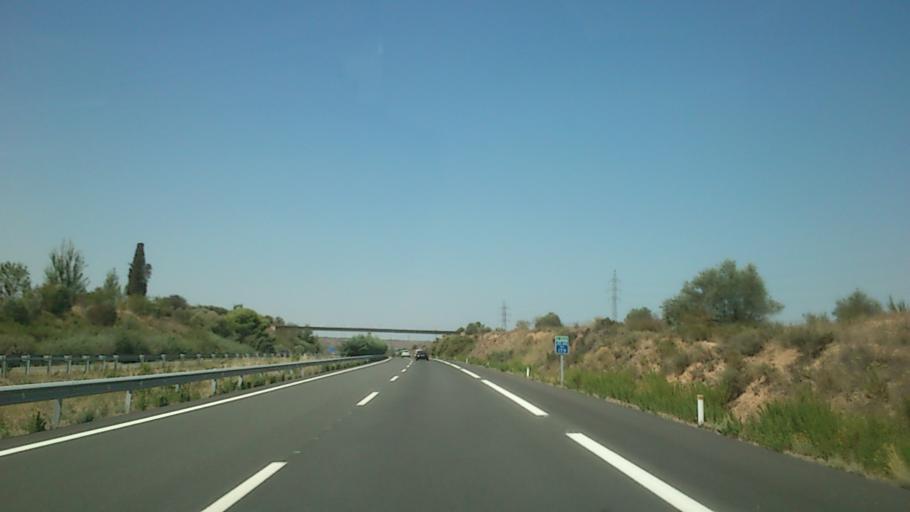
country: ES
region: La Rioja
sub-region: Provincia de La Rioja
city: Calahorra
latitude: 42.2839
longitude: -1.9453
